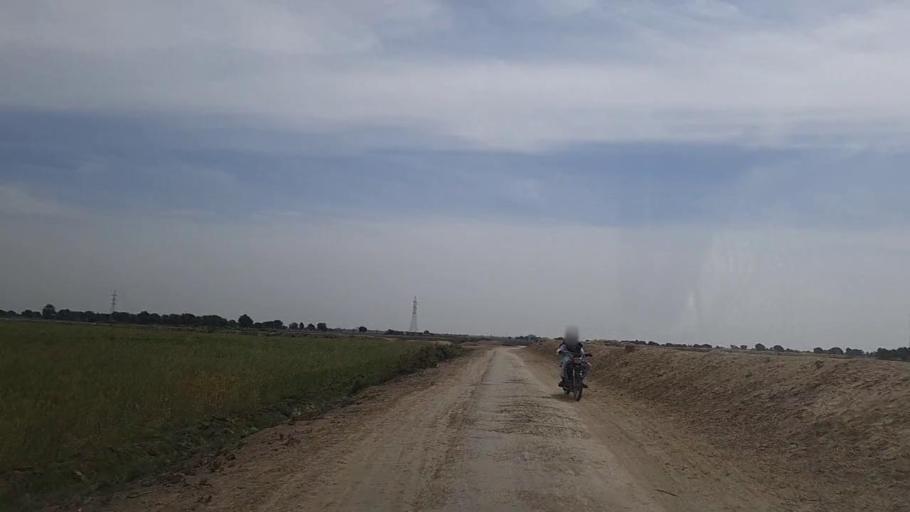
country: PK
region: Sindh
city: Samaro
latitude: 25.2966
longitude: 69.4532
